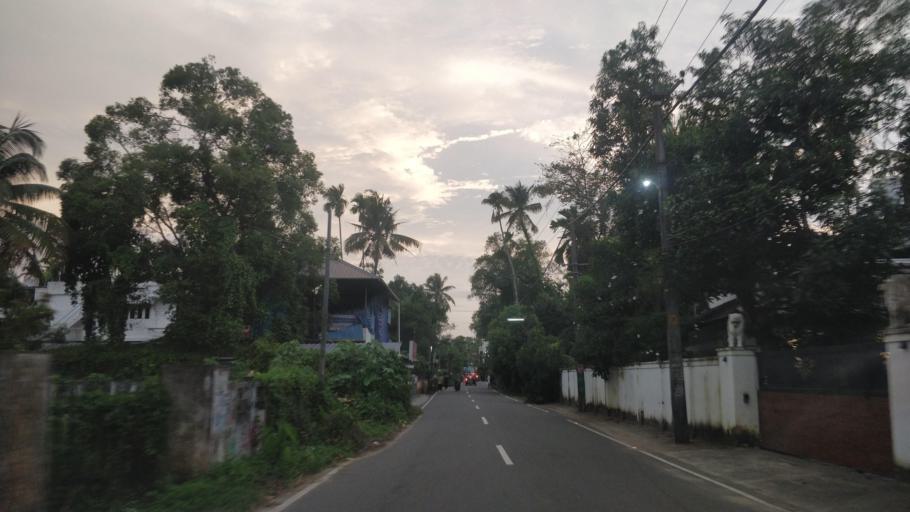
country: IN
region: Kerala
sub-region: Thrissur District
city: Kodungallur
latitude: 10.1421
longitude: 76.1897
